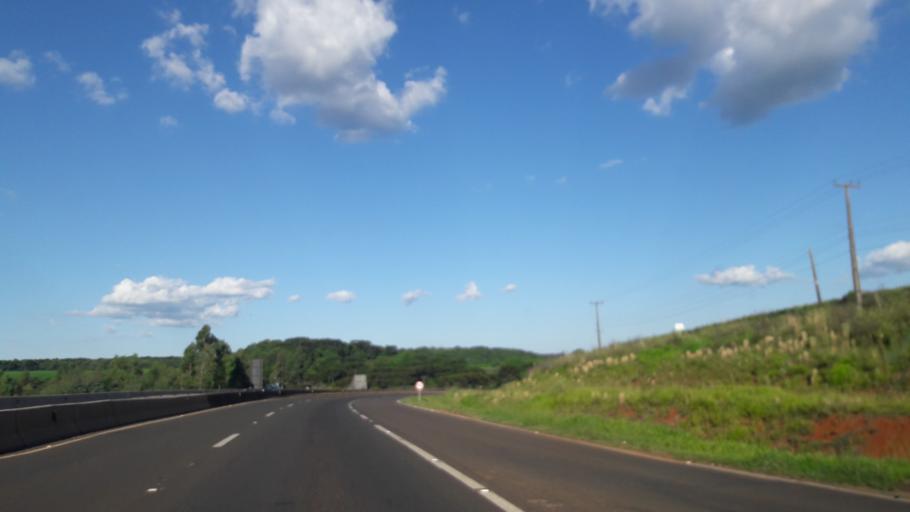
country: BR
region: Parana
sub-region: Guarapuava
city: Guarapuava
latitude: -25.3398
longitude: -51.4297
